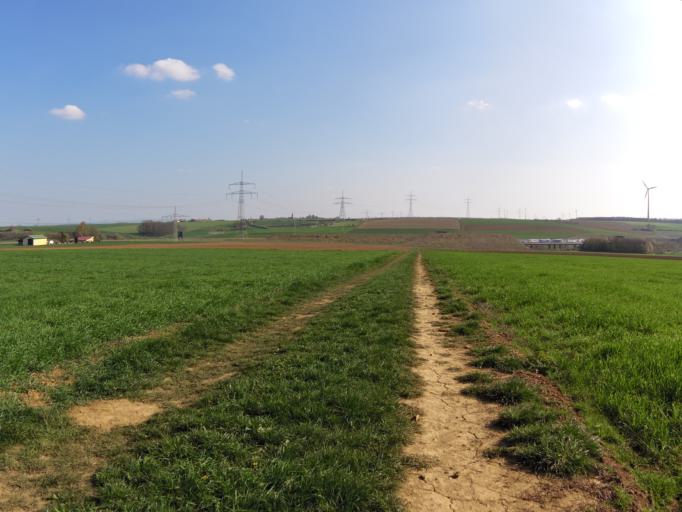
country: DE
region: Bavaria
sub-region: Regierungsbezirk Unterfranken
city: Theilheim
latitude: 49.7612
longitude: 10.0502
